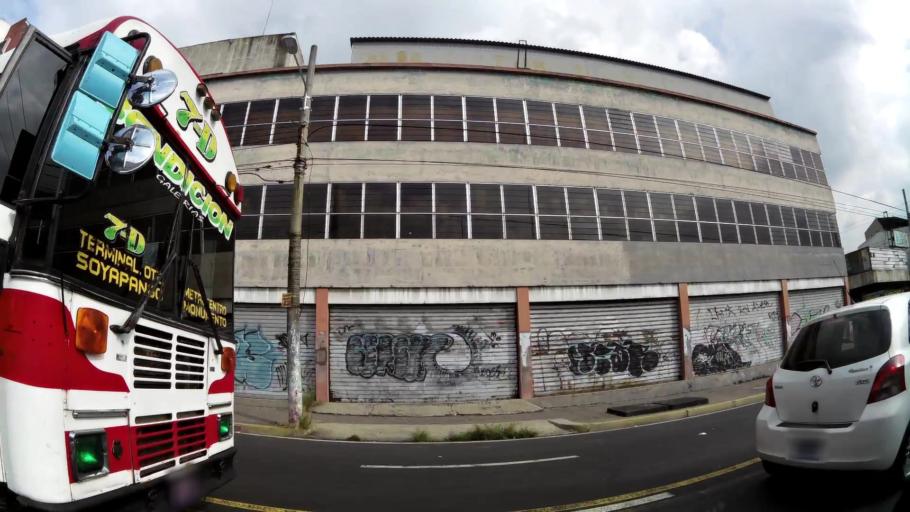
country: SV
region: San Salvador
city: San Salvador
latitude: 13.6991
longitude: -89.2016
